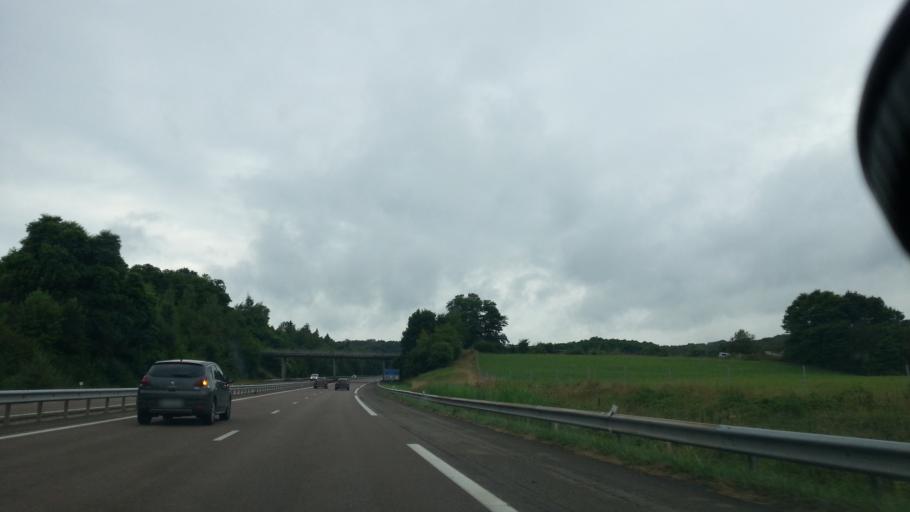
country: FR
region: Franche-Comte
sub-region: Departement du Jura
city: Orchamps
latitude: 47.1539
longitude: 5.6049
